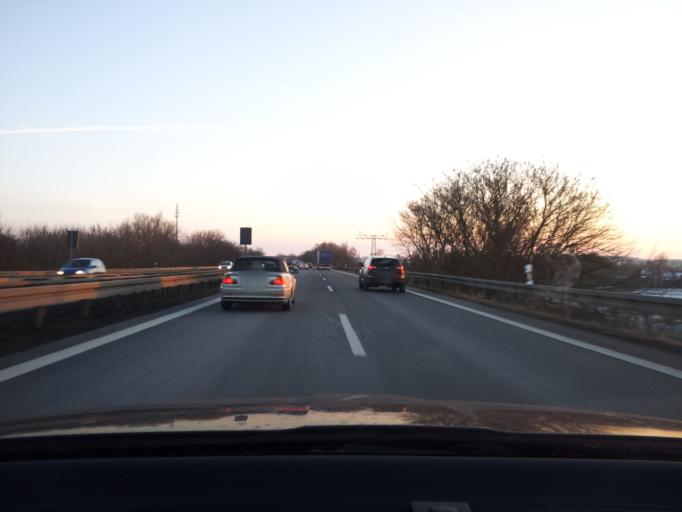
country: DE
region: Brandenburg
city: Wustermark
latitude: 52.5456
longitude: 12.9633
